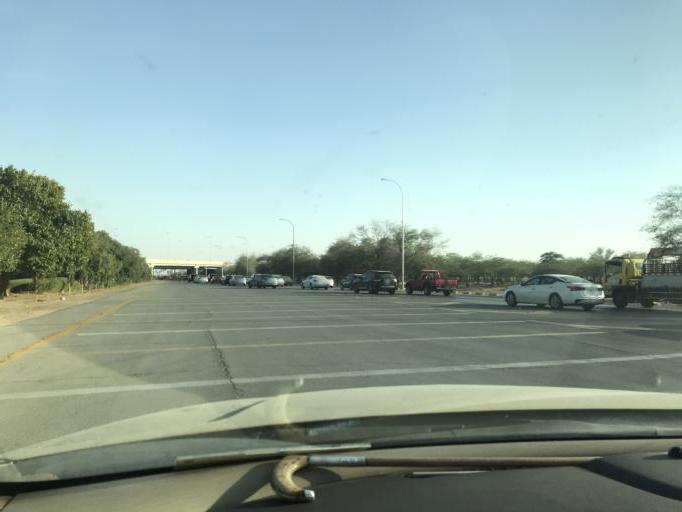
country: SA
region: Ar Riyad
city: Riyadh
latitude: 24.9477
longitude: 46.7049
